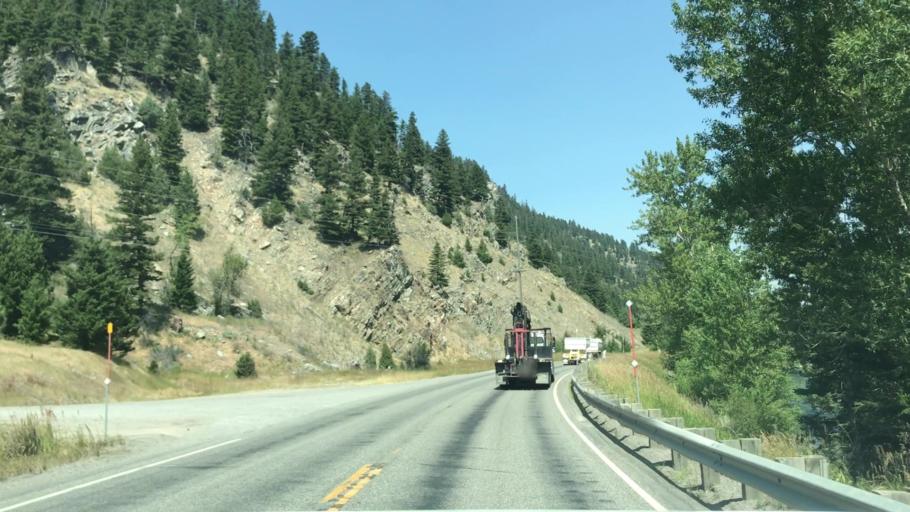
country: US
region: Montana
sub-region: Gallatin County
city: Four Corners
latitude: 45.5001
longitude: -111.2707
